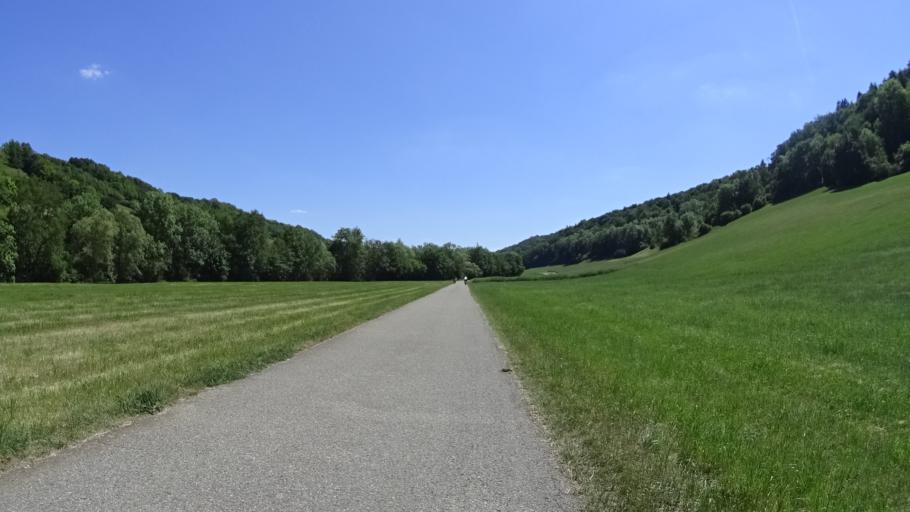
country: DE
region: Bavaria
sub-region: Regierungsbezirk Mittelfranken
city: Adelshofen
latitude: 49.4306
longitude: 10.1410
